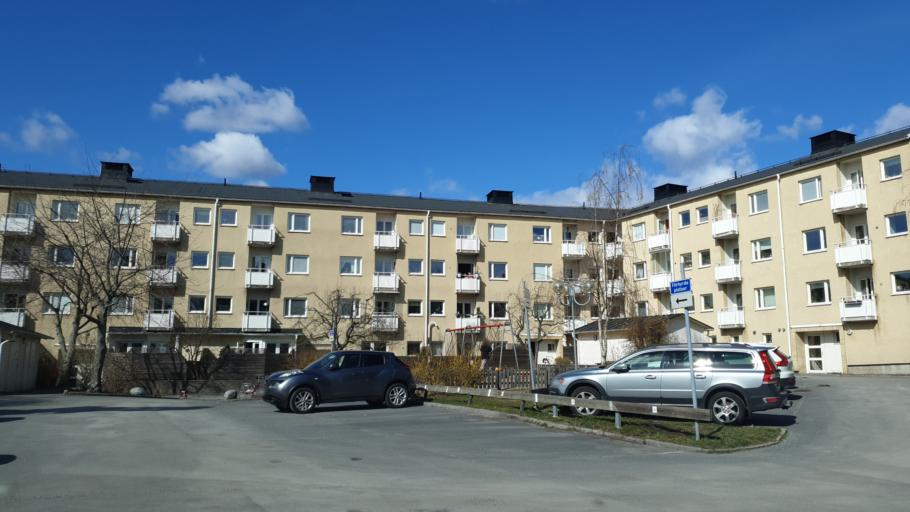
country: SE
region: Stockholm
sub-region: Nacka Kommun
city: Nacka
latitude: 59.3143
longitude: 18.1274
